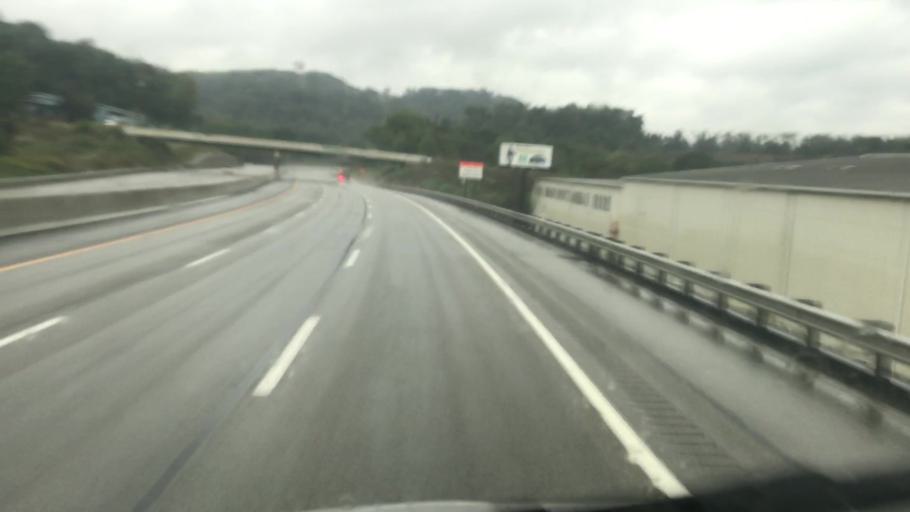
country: US
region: Pennsylvania
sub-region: Allegheny County
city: Oakmont
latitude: 40.5544
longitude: -79.8377
